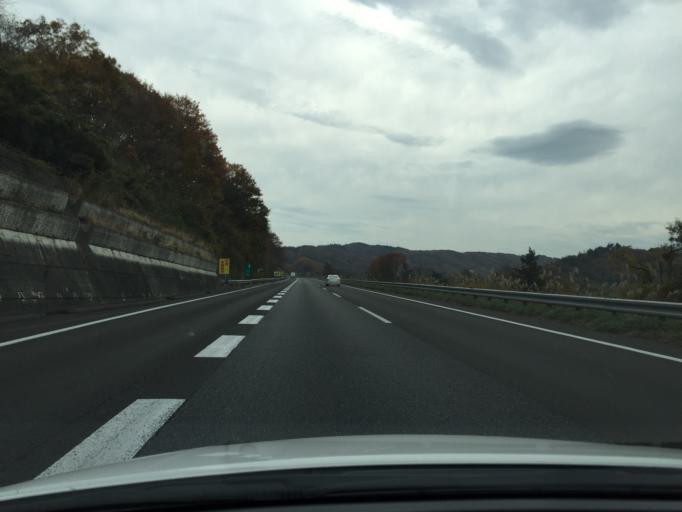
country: JP
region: Fukushima
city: Fukushima-shi
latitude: 37.6937
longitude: 140.4465
